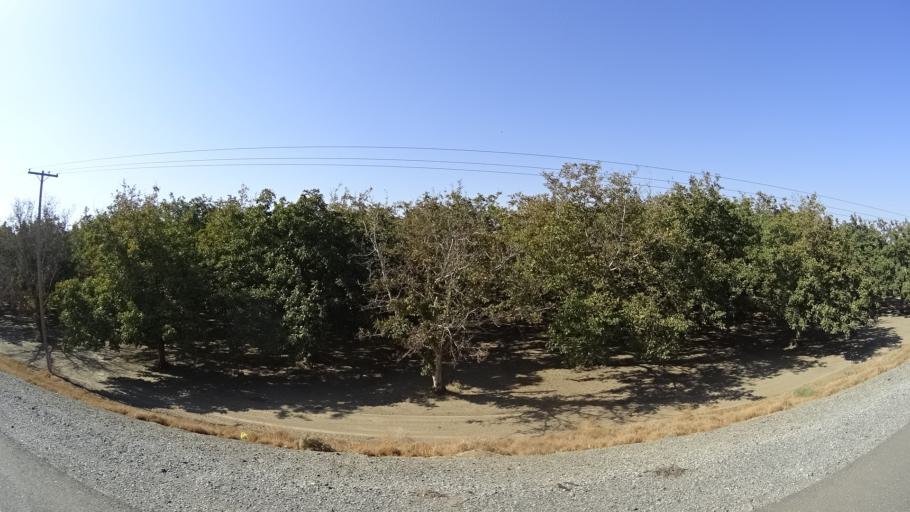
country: US
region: California
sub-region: Yolo County
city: West Sacramento
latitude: 38.6304
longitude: -121.5642
